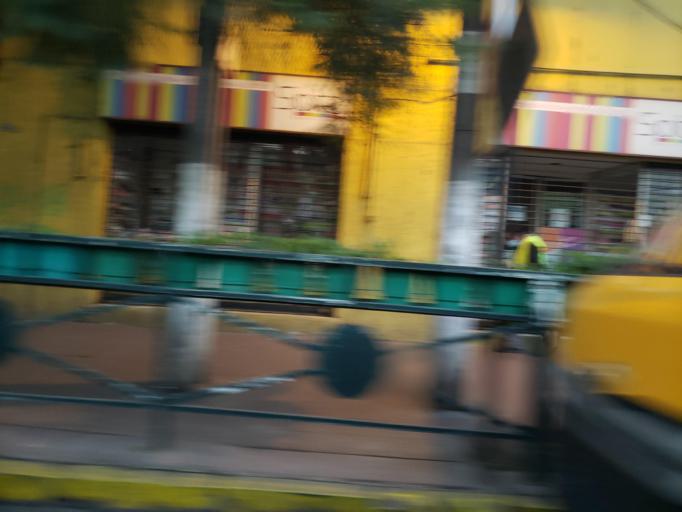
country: CL
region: Santiago Metropolitan
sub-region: Provincia de Talagante
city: Talagante
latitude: -33.6631
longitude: -70.9268
